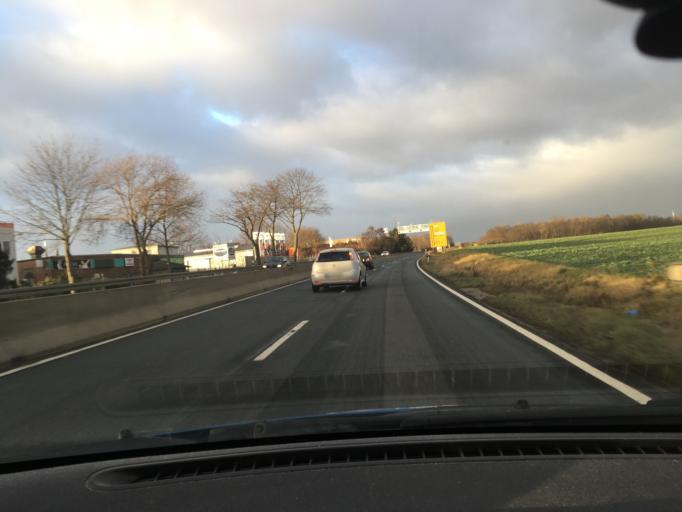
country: DE
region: Lower Saxony
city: Laatzen
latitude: 52.2937
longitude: 9.8315
